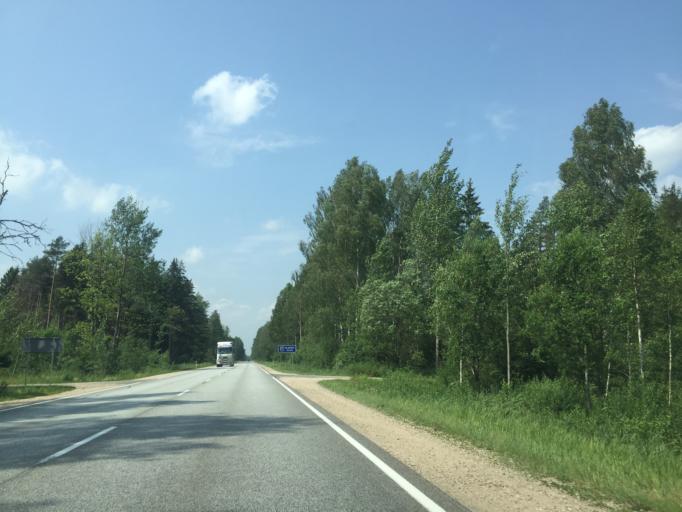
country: LV
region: Kekava
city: Balozi
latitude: 56.8147
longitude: 24.1388
